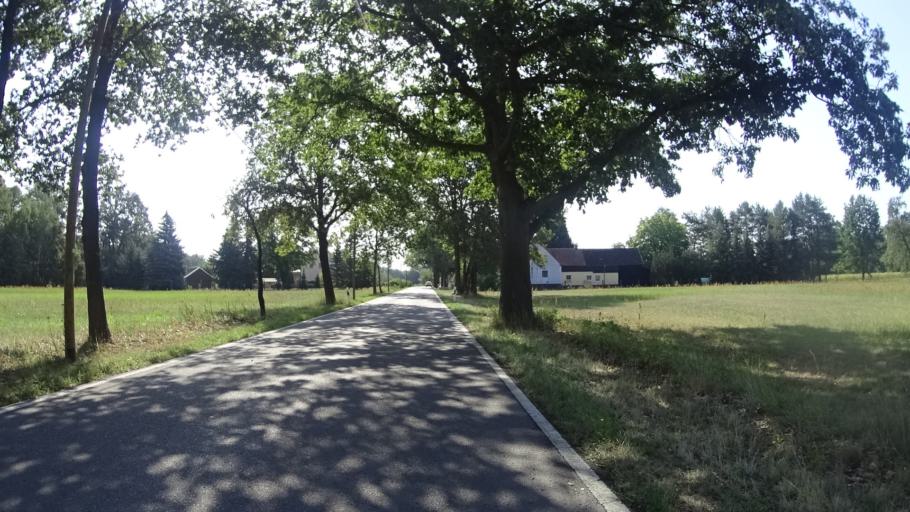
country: DE
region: Brandenburg
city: Burg
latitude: 51.8551
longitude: 14.1323
